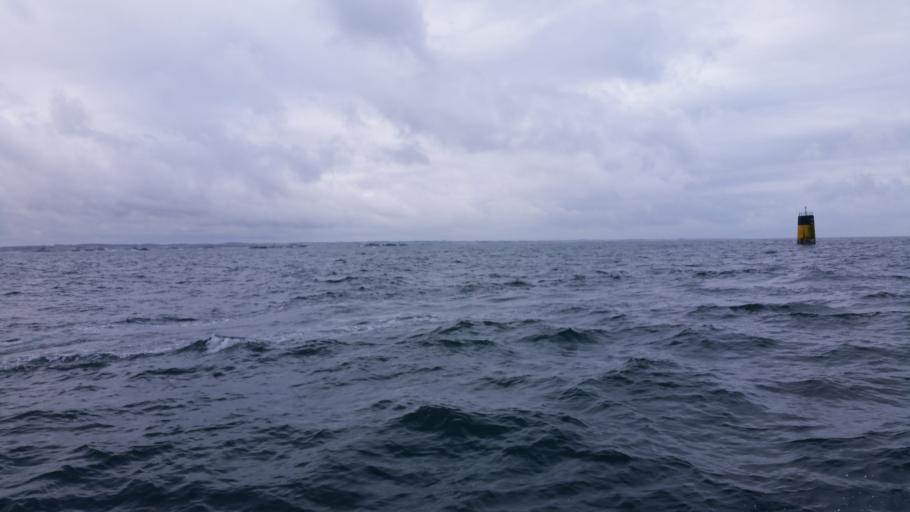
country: FR
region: Brittany
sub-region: Departement du Finistere
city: Santec
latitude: 48.7384
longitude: -4.0392
